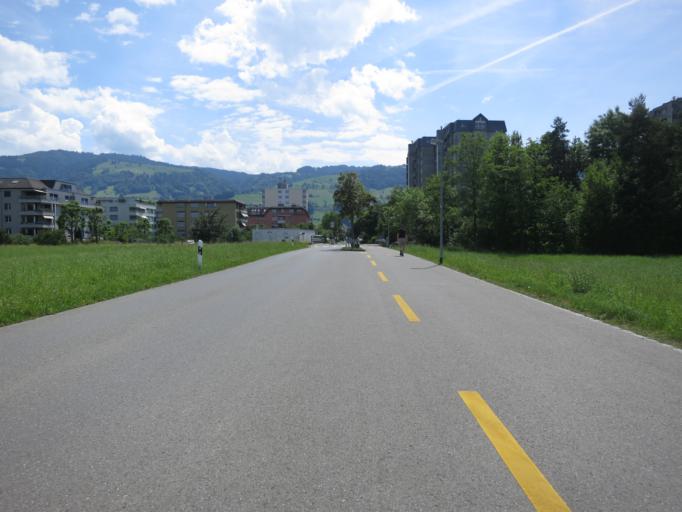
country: CH
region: Schwyz
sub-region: Bezirk March
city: Lachen
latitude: 47.1983
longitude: 8.8599
